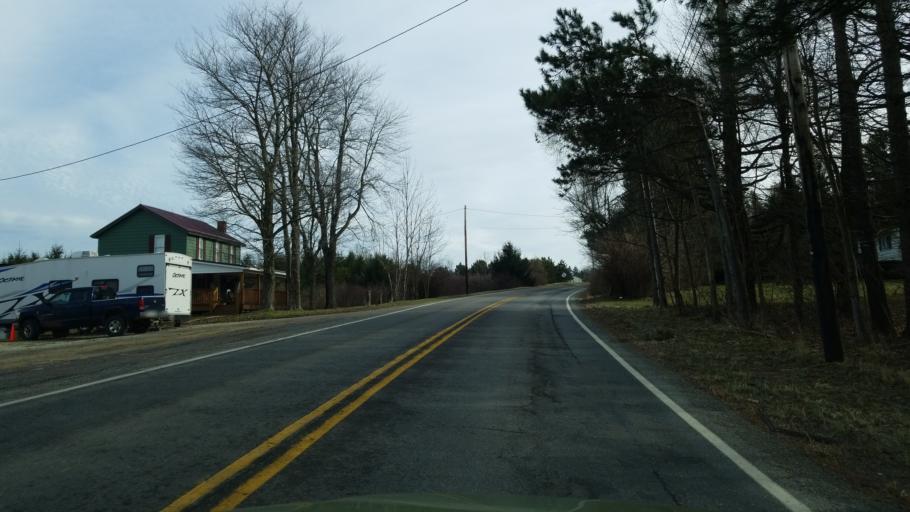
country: US
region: Pennsylvania
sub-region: Indiana County
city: Johnsonburg
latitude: 40.9155
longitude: -78.8305
